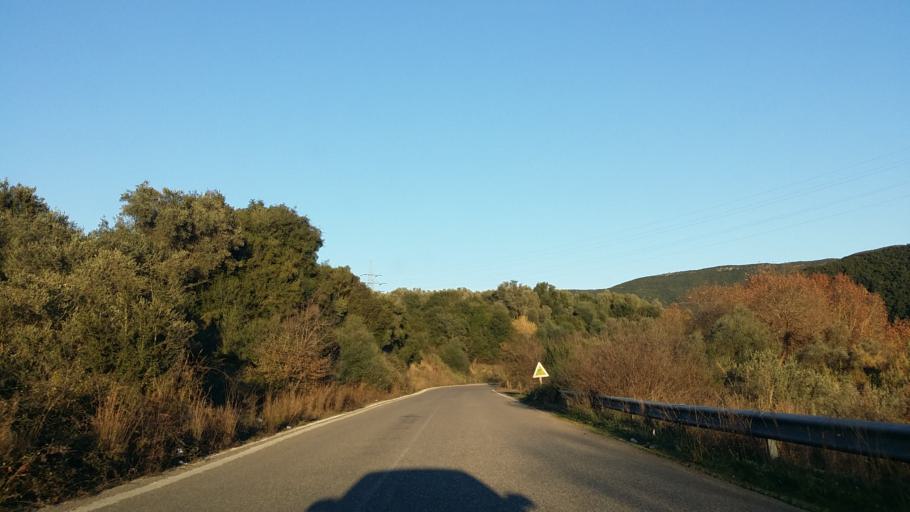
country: GR
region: West Greece
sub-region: Nomos Aitolias kai Akarnanias
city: Neapolis
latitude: 38.7095
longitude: 21.3473
